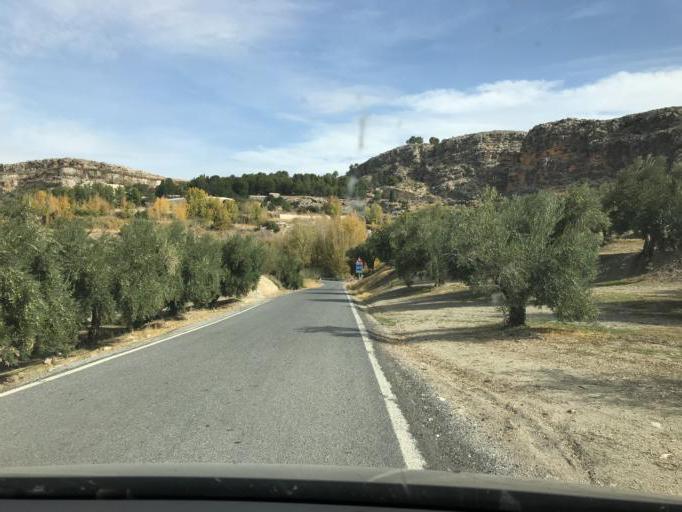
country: ES
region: Andalusia
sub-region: Provincia de Granada
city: Villanueva de las Torres
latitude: 37.5061
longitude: -3.1151
